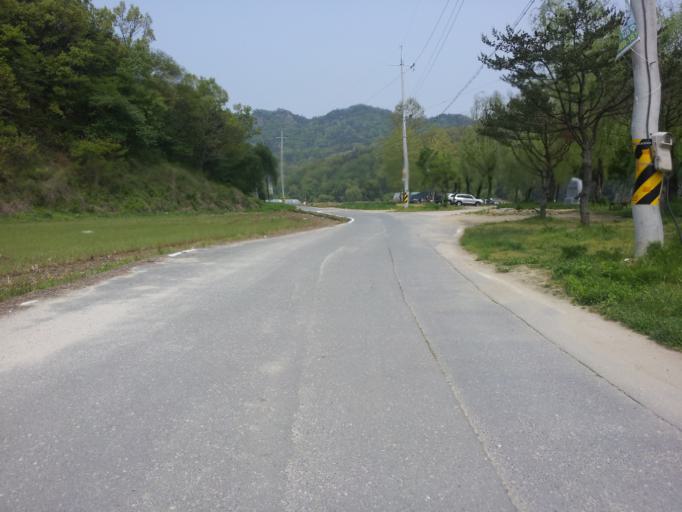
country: KR
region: Daejeon
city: Daejeon
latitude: 36.2760
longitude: 127.3435
